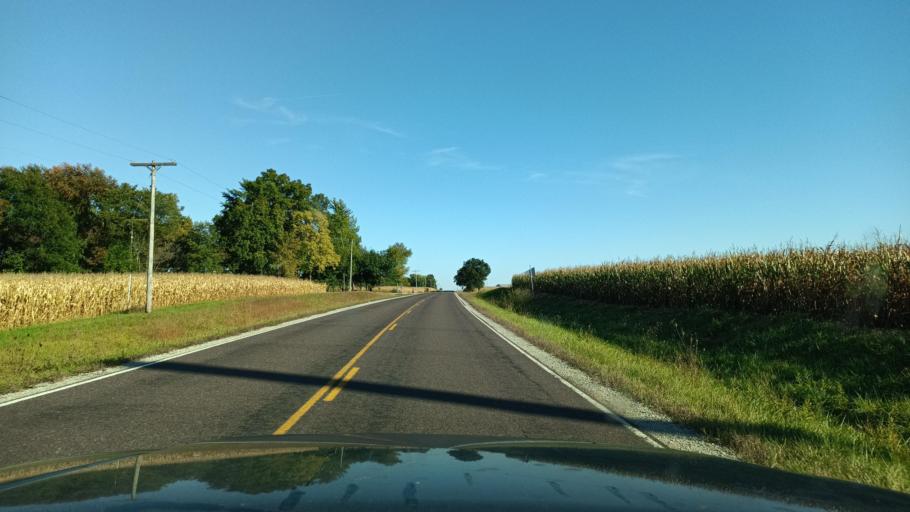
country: US
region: Illinois
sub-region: McLean County
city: Heyworth
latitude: 40.2374
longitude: -89.0781
